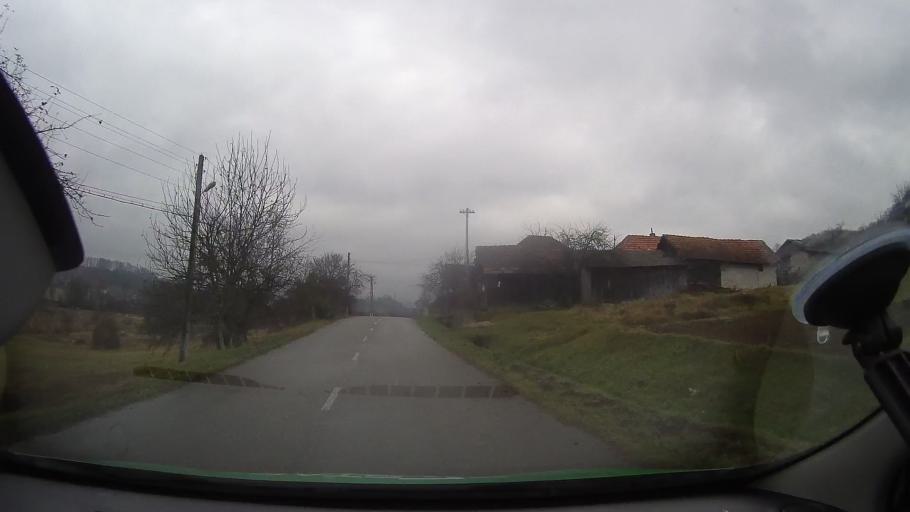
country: RO
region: Hunedoara
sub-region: Comuna Tomesti
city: Tomesti
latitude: 46.2098
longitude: 22.6647
